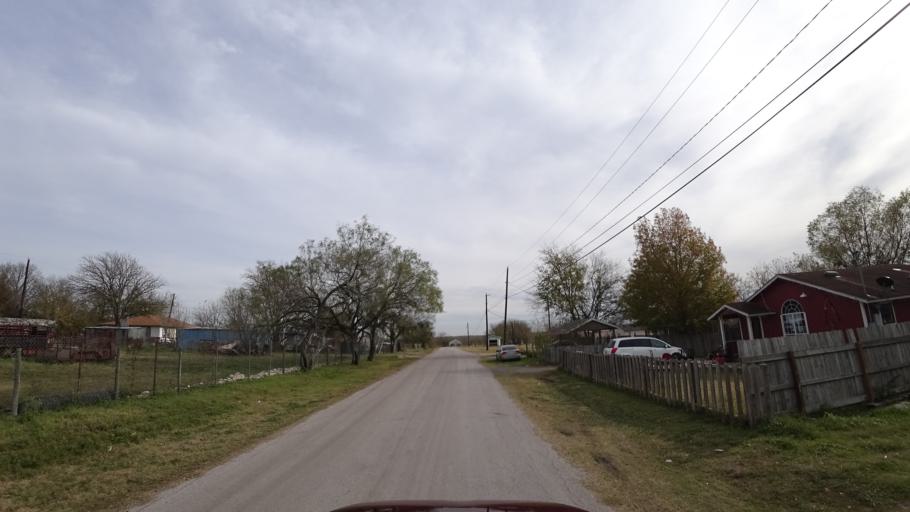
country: US
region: Texas
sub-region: Travis County
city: Garfield
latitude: 30.1300
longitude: -97.6223
